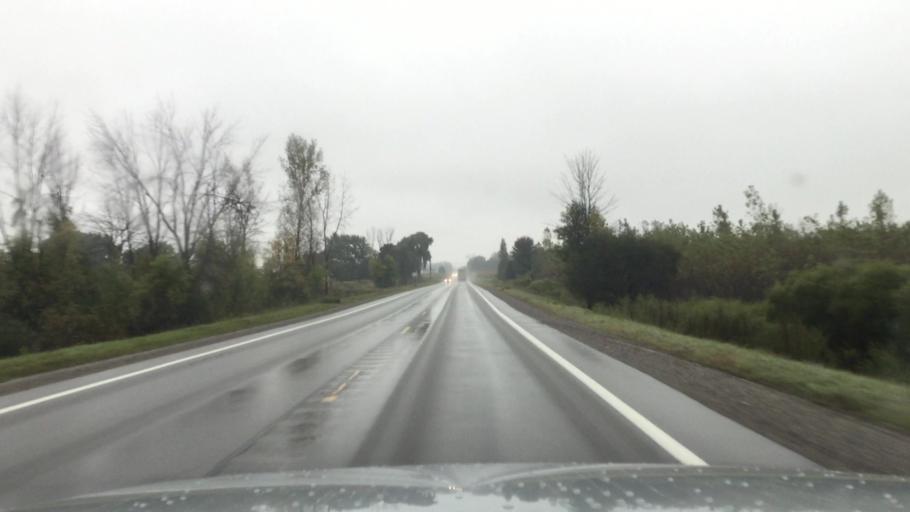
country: US
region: Michigan
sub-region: Saginaw County
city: Saginaw
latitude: 43.3617
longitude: -83.9548
